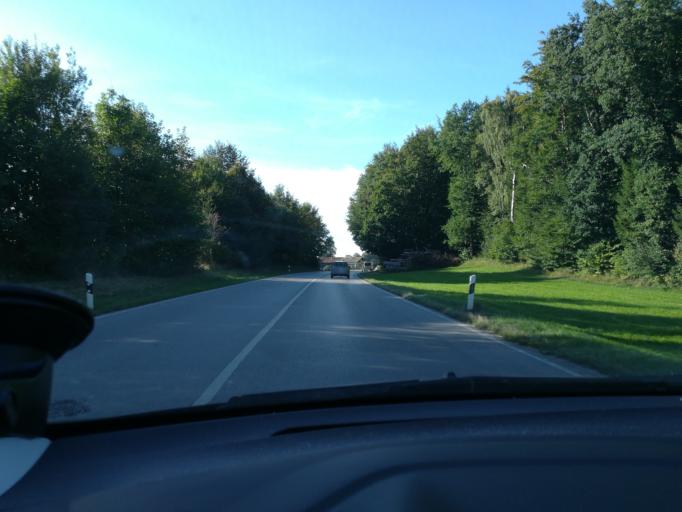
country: DE
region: Bavaria
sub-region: Upper Bavaria
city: Miesbach
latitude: 47.7969
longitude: 11.8388
